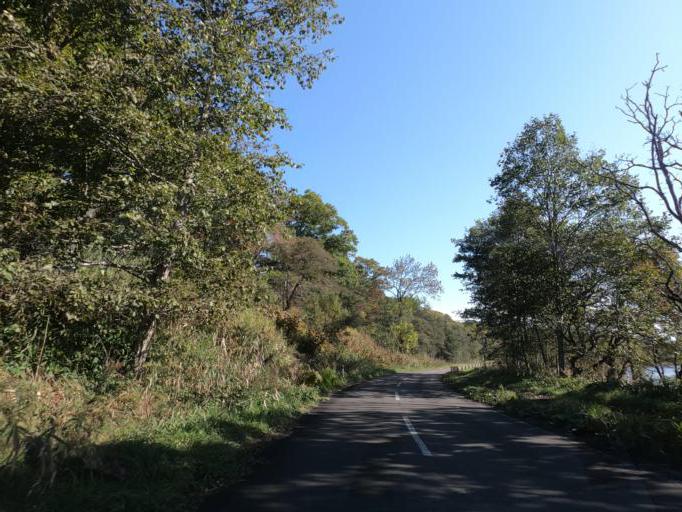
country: JP
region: Hokkaido
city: Obihiro
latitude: 42.6078
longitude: 143.5494
